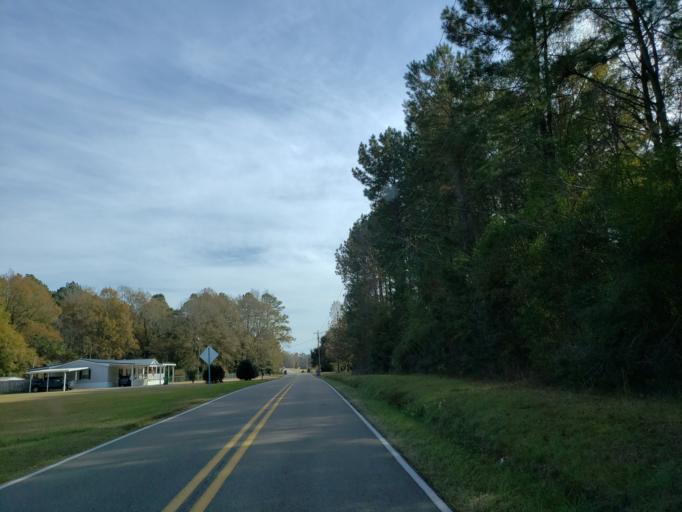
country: US
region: Mississippi
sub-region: Forrest County
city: Rawls Springs
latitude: 31.3991
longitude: -89.3620
